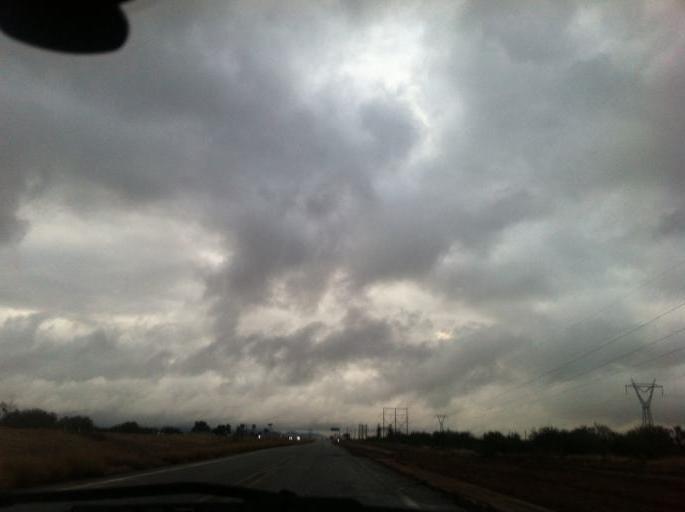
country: MX
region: Sonora
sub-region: San Miguel de Horcasitas
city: Las Mercedes [Agropecuaria]
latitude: 29.6842
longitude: -111.0424
